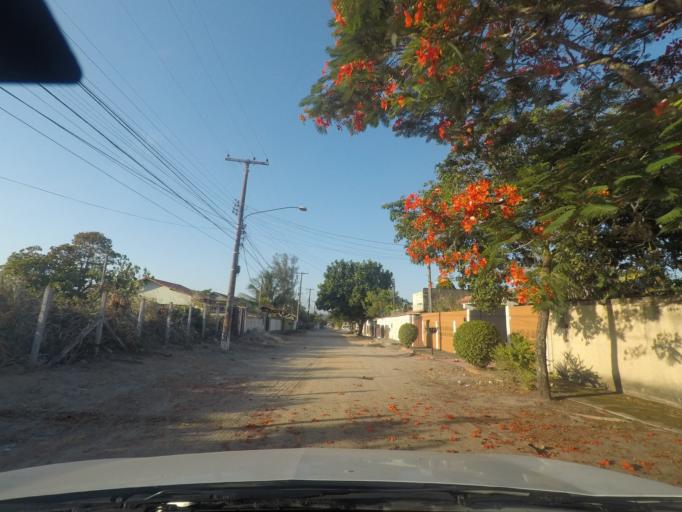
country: BR
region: Rio de Janeiro
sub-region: Marica
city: Marica
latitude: -22.9685
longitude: -42.9316
